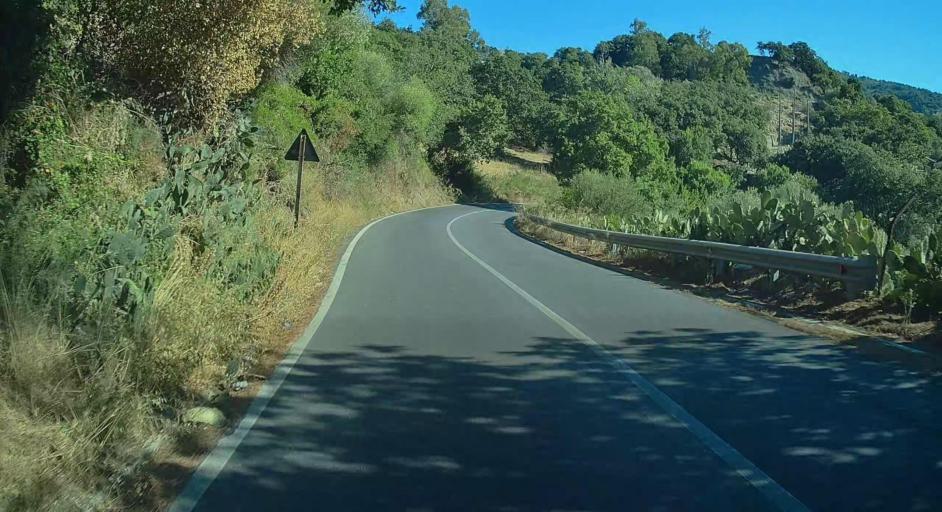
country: IT
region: Sicily
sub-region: Messina
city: Oliveri
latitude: 38.1364
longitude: 15.0350
